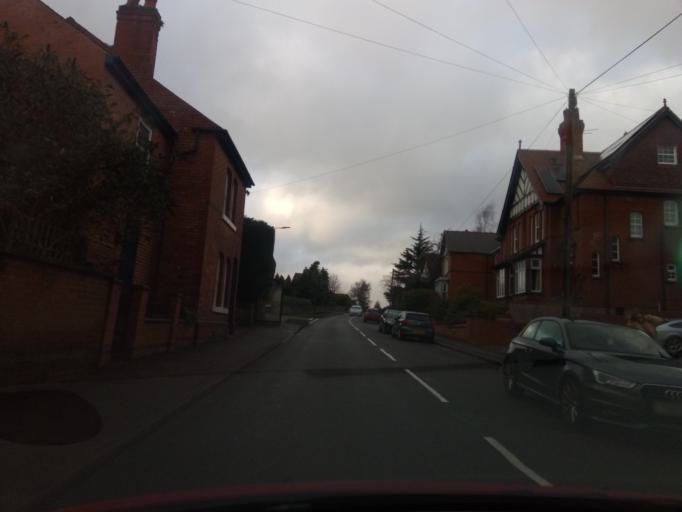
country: GB
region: England
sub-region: Derbyshire
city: Melbourne
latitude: 52.8269
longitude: -1.4313
